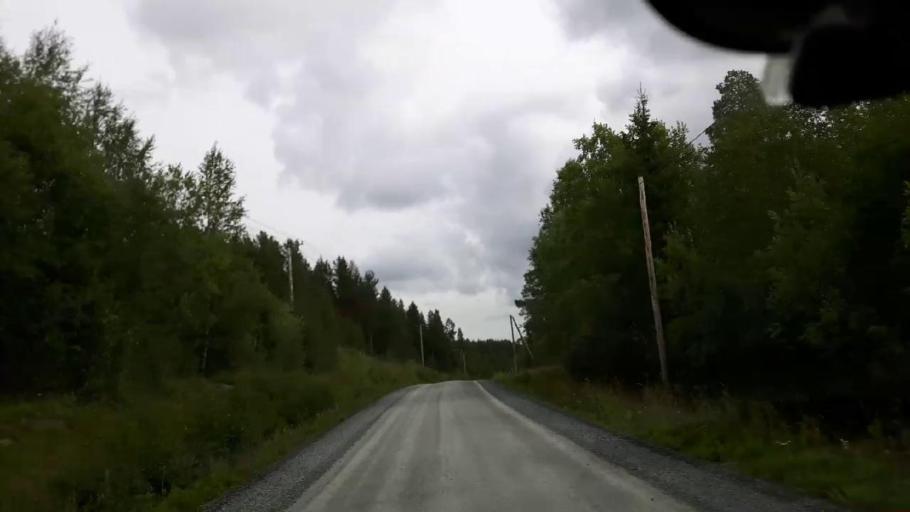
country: SE
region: Jaemtland
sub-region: Krokoms Kommun
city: Krokom
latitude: 63.5787
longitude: 14.2169
